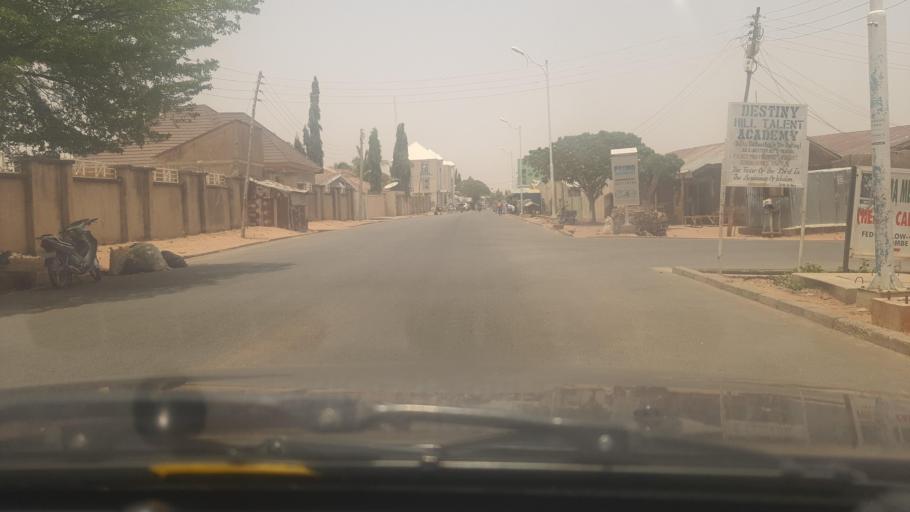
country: NG
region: Gombe
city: Gombe
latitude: 10.3016
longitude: 11.1468
